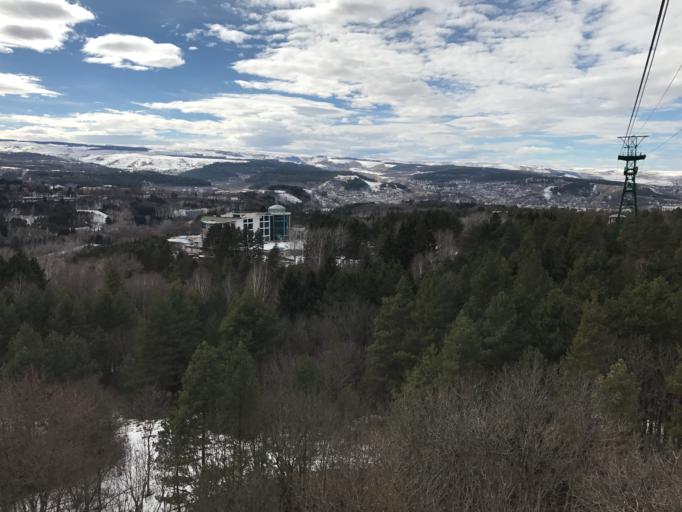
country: RU
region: Stavropol'skiy
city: Kislovodsk
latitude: 43.8981
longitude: 42.7439
